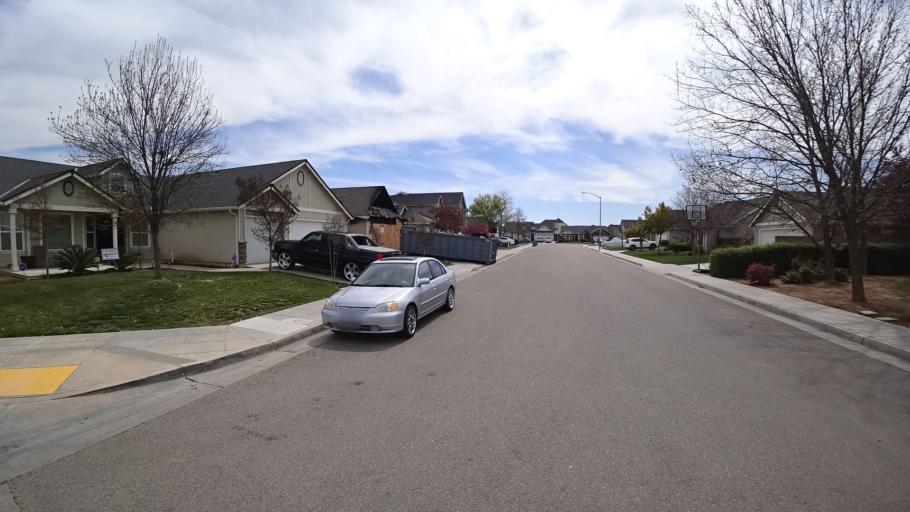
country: US
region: California
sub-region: Fresno County
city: Biola
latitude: 36.8143
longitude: -119.9172
